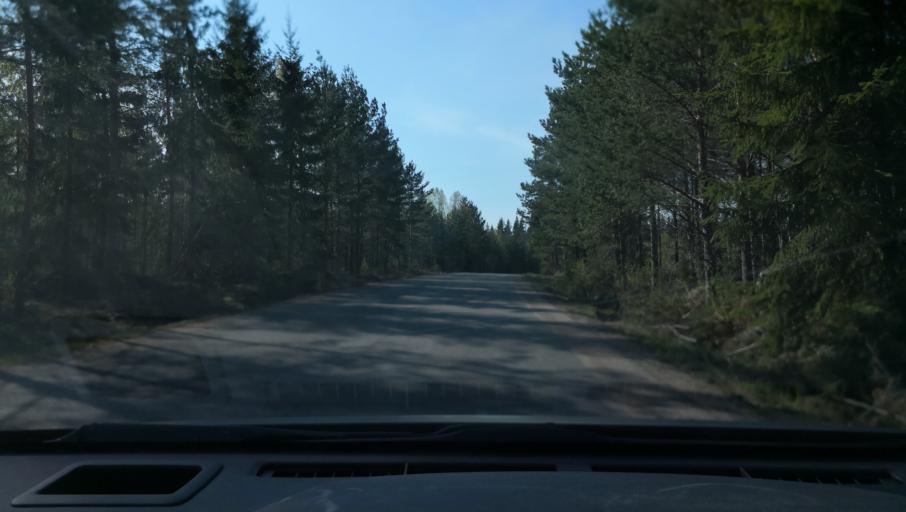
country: SE
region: Uppsala
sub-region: Heby Kommun
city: Tarnsjo
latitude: 60.2592
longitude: 16.9445
